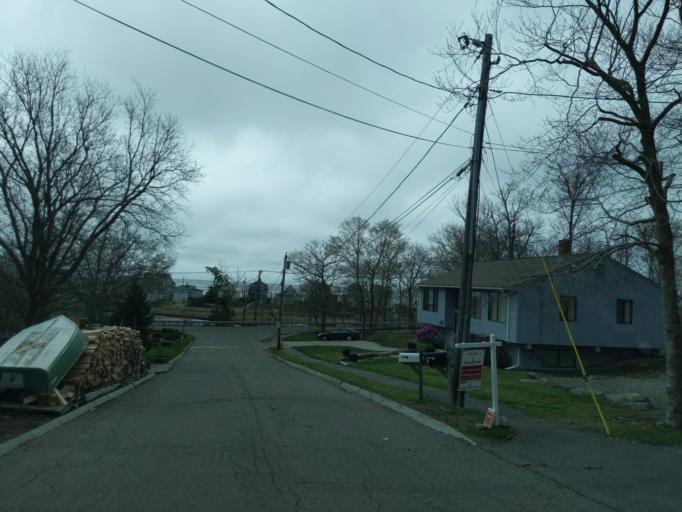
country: US
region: Massachusetts
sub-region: Essex County
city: Rockport
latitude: 42.6340
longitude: -70.6154
